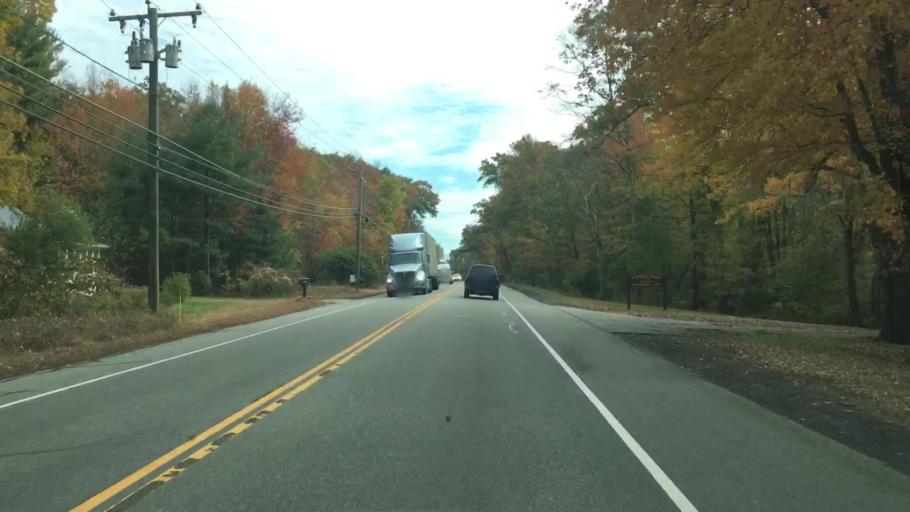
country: US
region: Connecticut
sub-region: Tolland County
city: Crystal Lake
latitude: 41.9769
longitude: -72.3873
